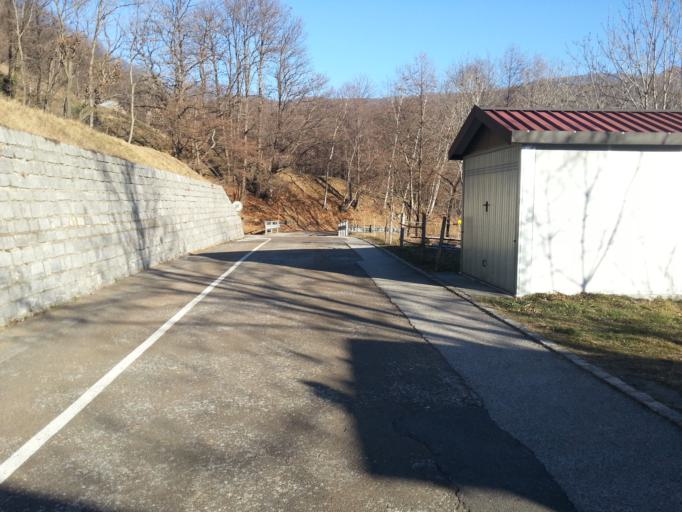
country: CH
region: Ticino
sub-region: Bellinzona District
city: Cadenazzo
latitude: 46.1215
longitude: 8.9570
